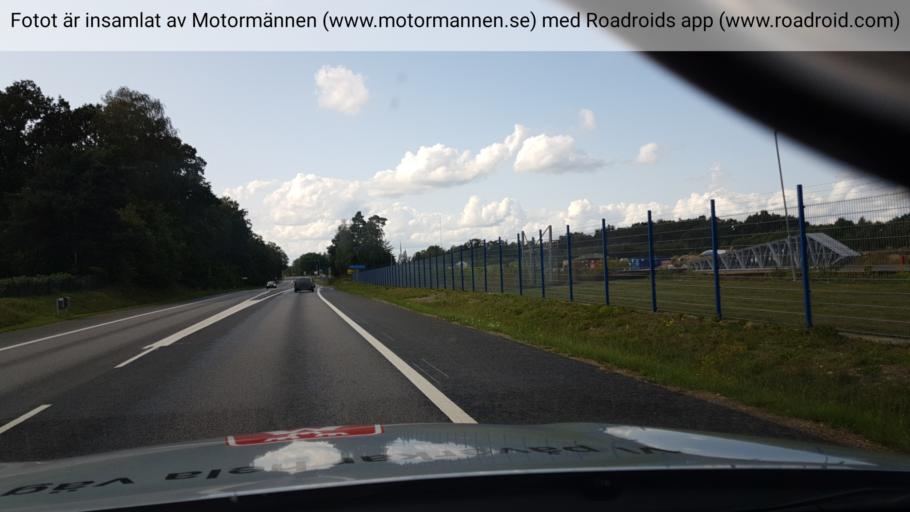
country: SE
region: Skane
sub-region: Hassleholms Kommun
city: Hassleholm
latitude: 56.1427
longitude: 13.7988
